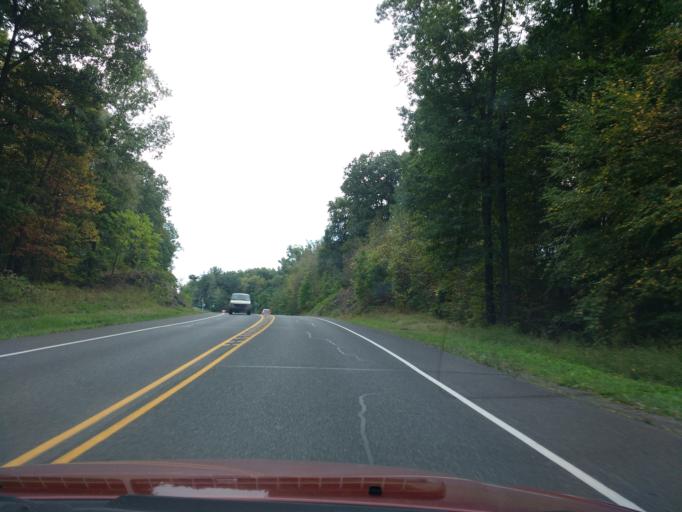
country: US
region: New York
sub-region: Ulster County
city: Lincoln Park
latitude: 41.9542
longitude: -73.9791
